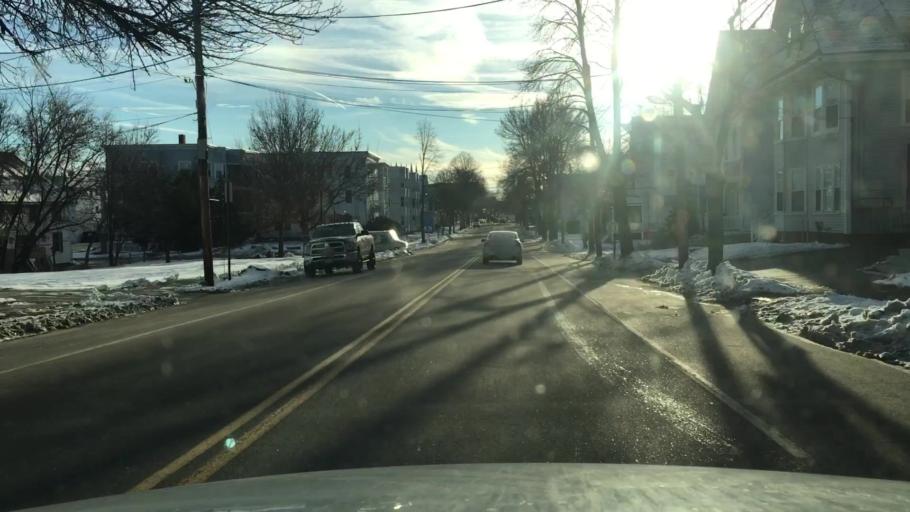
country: US
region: Maine
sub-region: Androscoggin County
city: Lewiston
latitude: 44.1044
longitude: -70.2081
